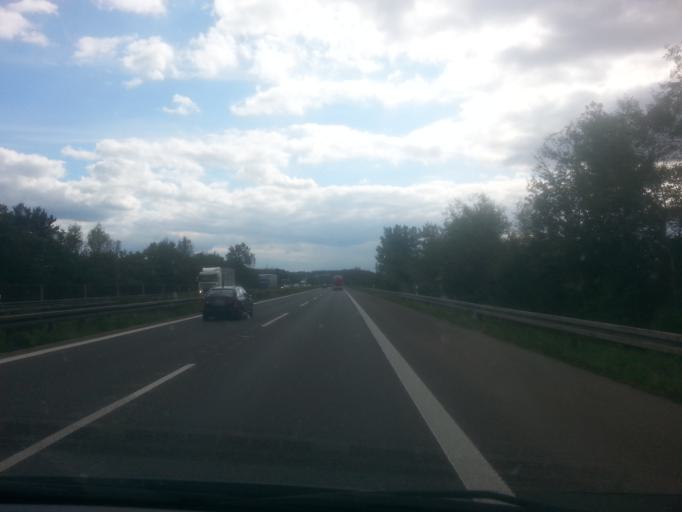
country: DE
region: Bavaria
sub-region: Upper Palatinate
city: Stulln
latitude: 49.4102
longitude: 12.1640
